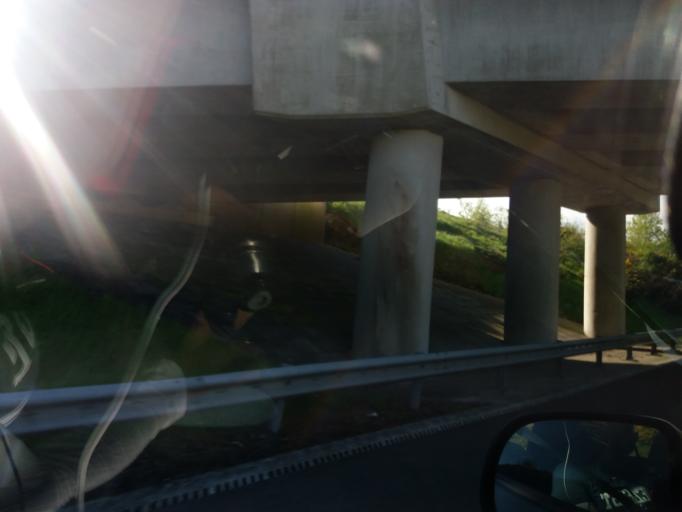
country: IE
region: Leinster
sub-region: Kilkenny
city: Mooncoin
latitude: 52.3735
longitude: -7.1670
